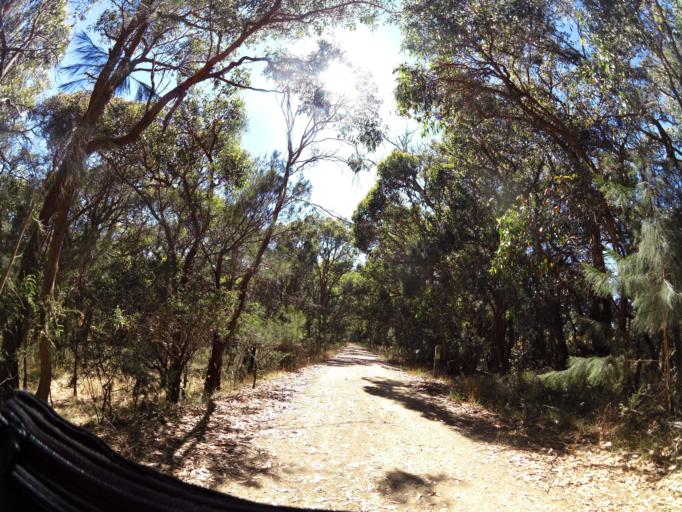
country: AU
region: Victoria
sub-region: Ballarat North
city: Delacombe
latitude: -37.6644
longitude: 143.4992
